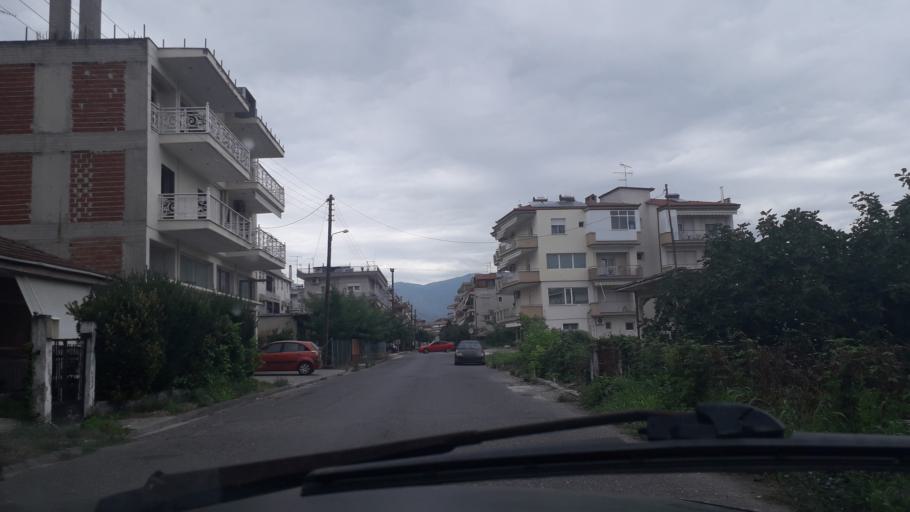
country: GR
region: Central Macedonia
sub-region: Nomos Pellis
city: Aridaia
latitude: 40.9695
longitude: 22.0633
